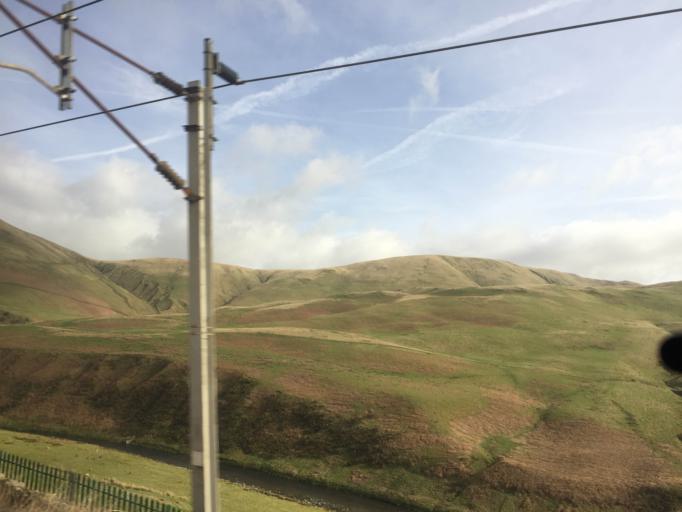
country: GB
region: England
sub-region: Cumbria
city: Sedbergh
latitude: 54.3834
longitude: -2.5813
